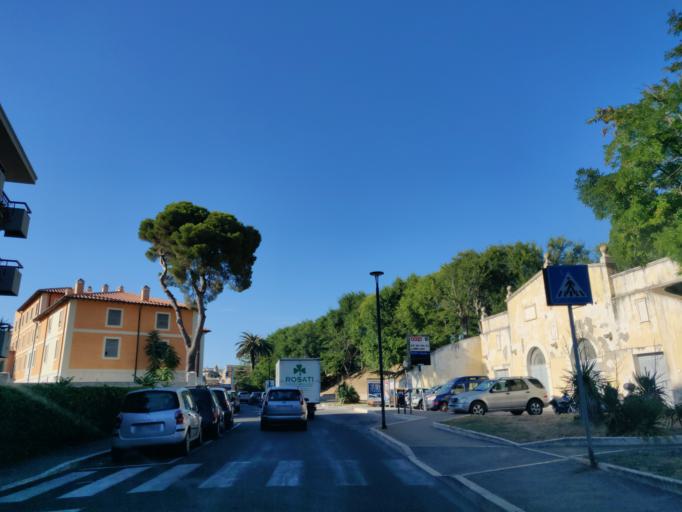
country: IT
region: Tuscany
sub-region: Provincia di Grosseto
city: Orbetello
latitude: 42.4383
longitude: 11.2143
